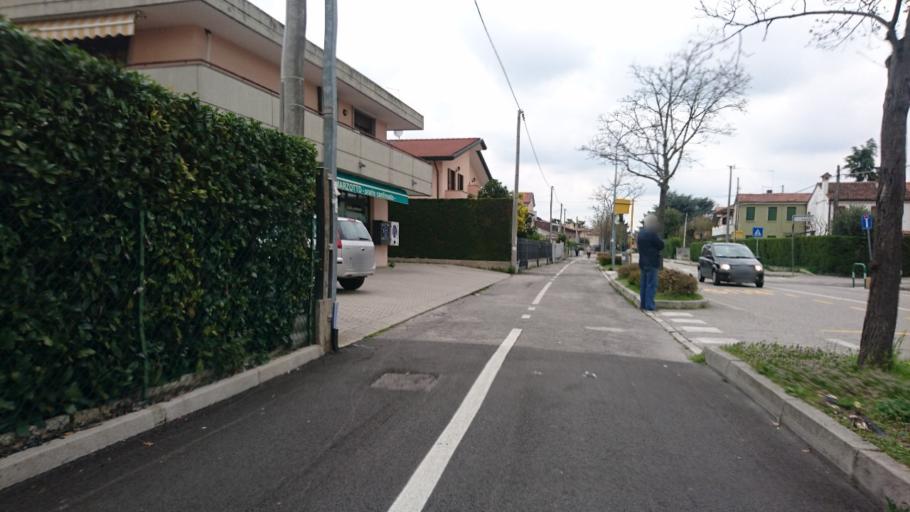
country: IT
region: Veneto
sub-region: Provincia di Padova
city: Vigodarzere
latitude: 45.4394
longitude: 11.8704
